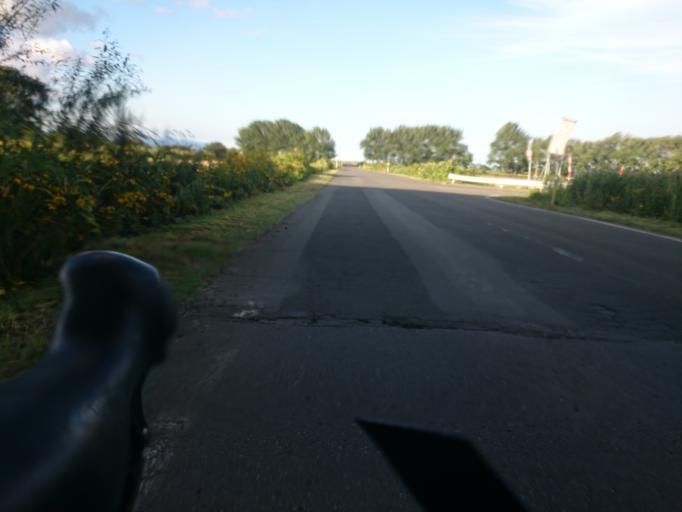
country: JP
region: Hokkaido
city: Tobetsu
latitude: 43.1835
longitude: 141.5584
